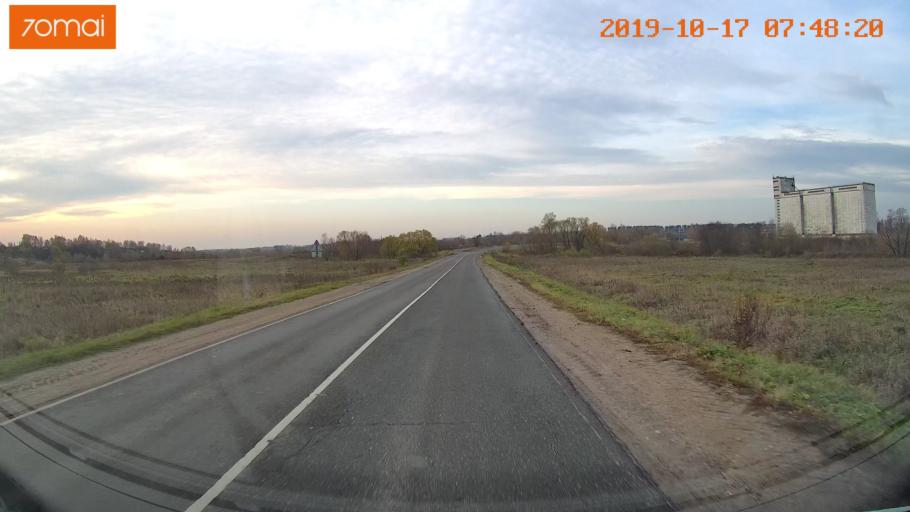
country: RU
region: Vladimir
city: Yur'yev-Pol'skiy
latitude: 56.4808
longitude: 39.6761
